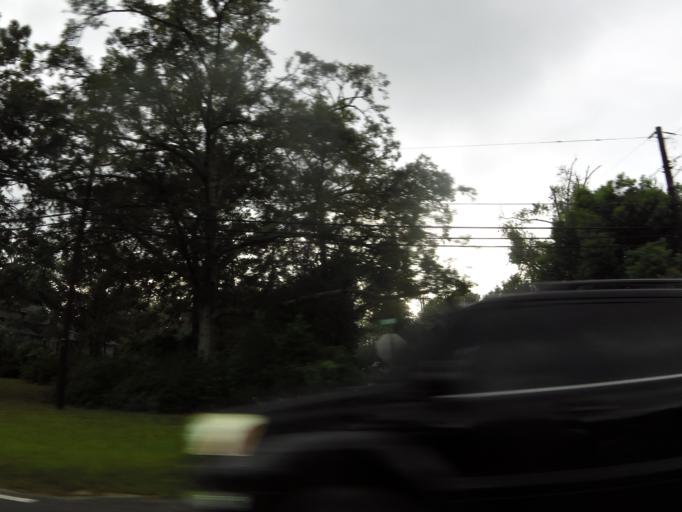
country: US
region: Georgia
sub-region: Wayne County
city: Jesup
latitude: 31.5972
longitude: -81.8733
